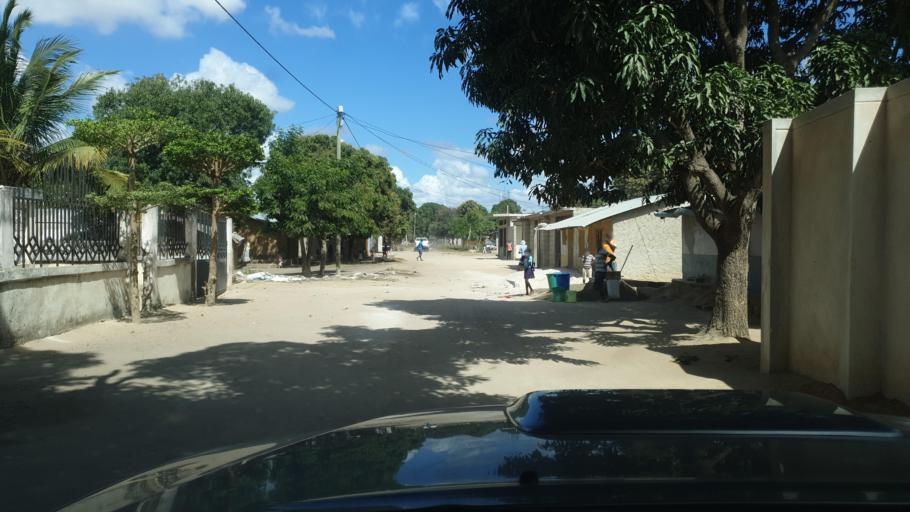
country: MZ
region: Nampula
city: Nacala
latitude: -14.5706
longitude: 40.6984
